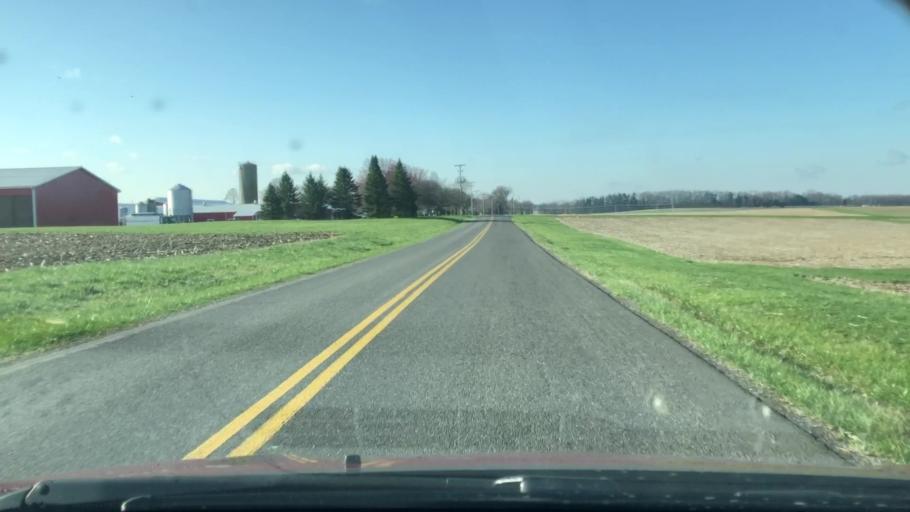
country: US
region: Ohio
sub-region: Wayne County
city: Wooster
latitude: 40.7741
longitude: -81.9058
